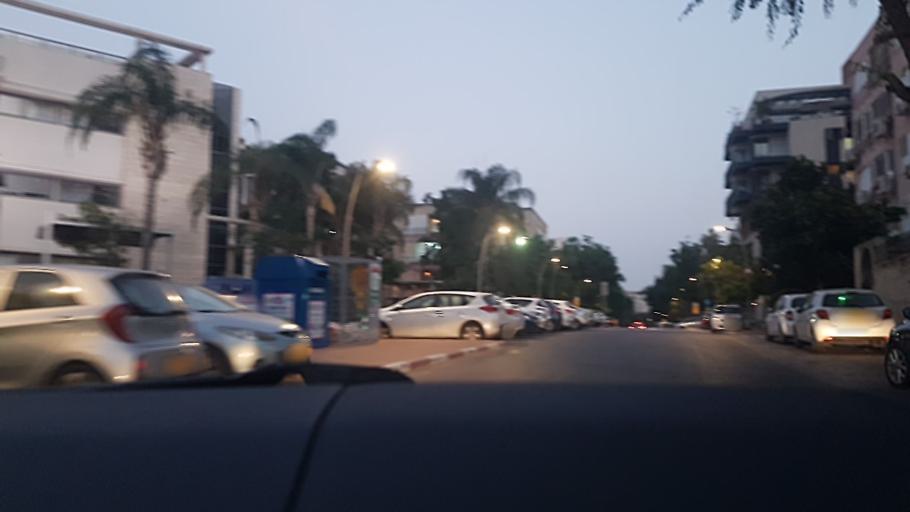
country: IL
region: Tel Aviv
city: Ramat Gan
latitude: 32.0823
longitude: 34.8035
